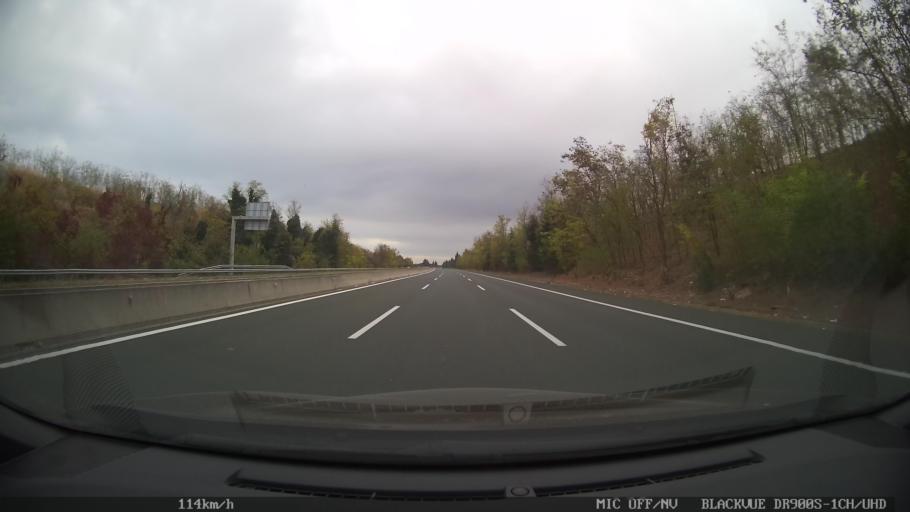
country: GR
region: Central Macedonia
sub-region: Nomos Pierias
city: Makrygialos
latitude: 40.4059
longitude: 22.5955
